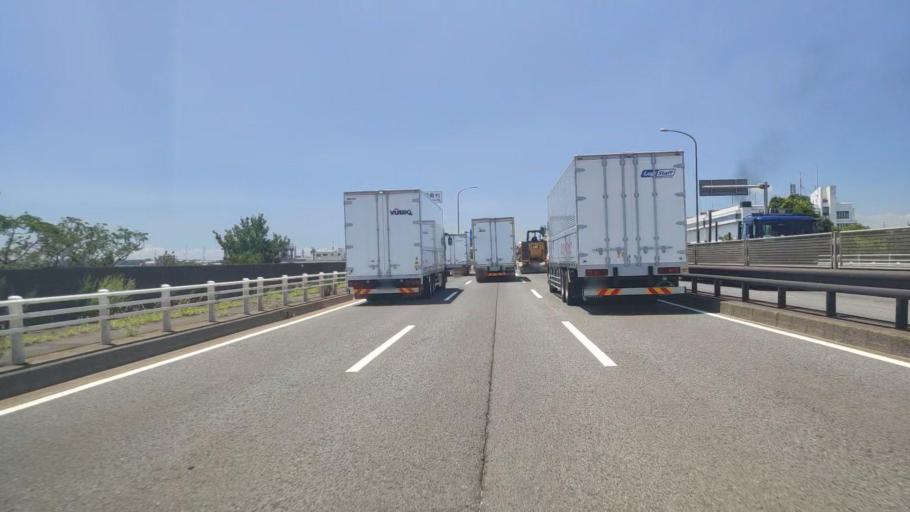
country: JP
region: Aichi
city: Kanie
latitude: 35.0812
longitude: 136.8255
